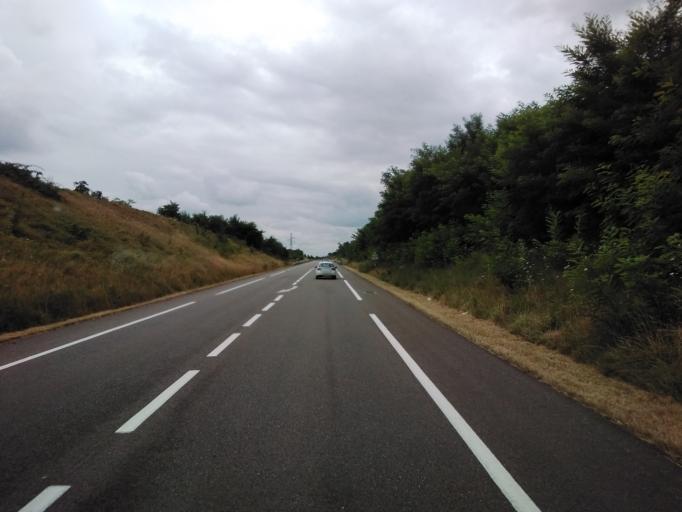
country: FR
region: Franche-Comte
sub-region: Departement du Jura
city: Montmorot
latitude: 46.6695
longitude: 5.5079
